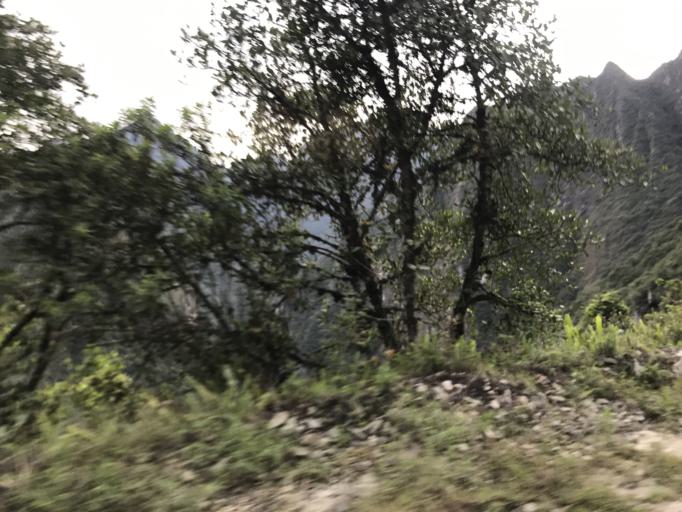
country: PE
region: Cusco
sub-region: Provincia de La Convencion
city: Santa Teresa
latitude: -13.1663
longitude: -72.5397
